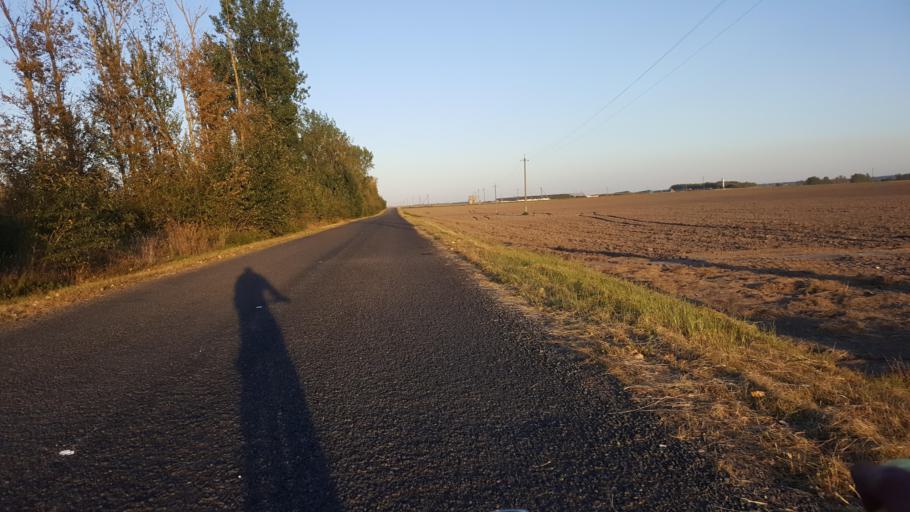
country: BY
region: Brest
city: Vysokaye
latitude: 52.2967
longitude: 23.5261
